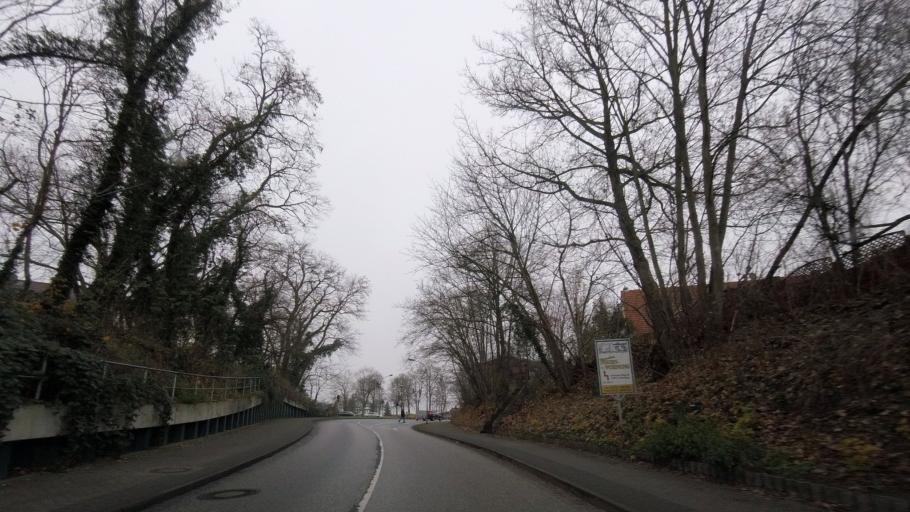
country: DE
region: Brandenburg
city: Juterbog
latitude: 52.0016
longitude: 13.0864
